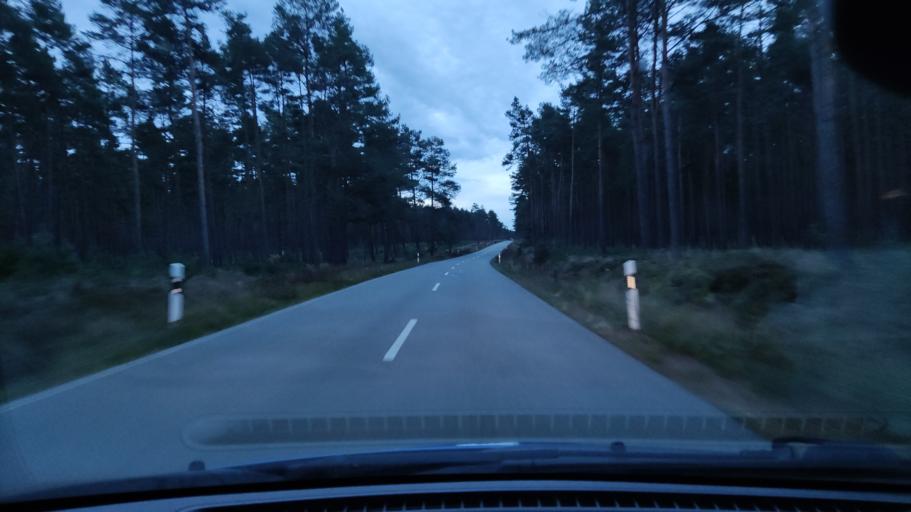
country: DE
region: Lower Saxony
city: Prezelle
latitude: 52.9923
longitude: 11.3951
